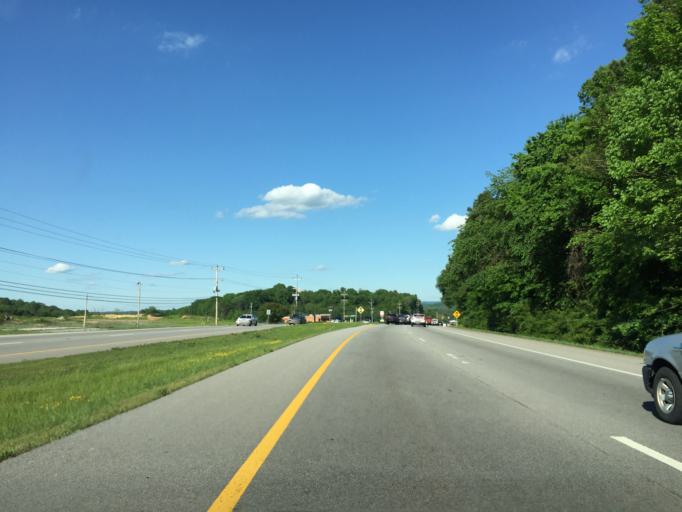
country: US
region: Tennessee
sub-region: Hamilton County
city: Harrison
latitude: 35.1033
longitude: -85.1645
